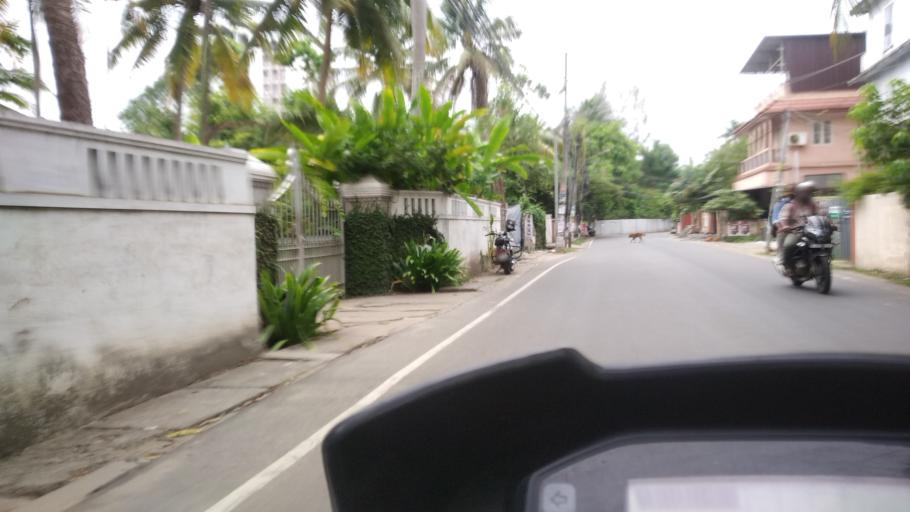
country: IN
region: Kerala
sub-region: Ernakulam
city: Cochin
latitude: 9.9567
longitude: 76.3023
